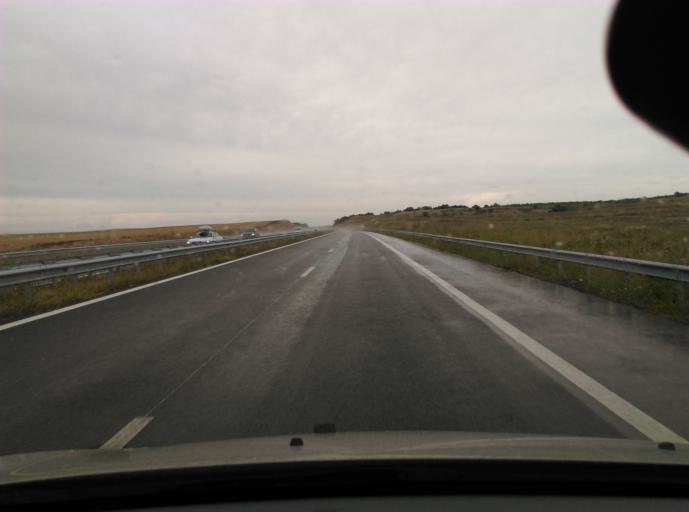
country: BG
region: Khaskovo
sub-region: Obshtina Dimitrovgrad
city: Dimitrovgrad
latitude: 42.0397
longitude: 25.5300
